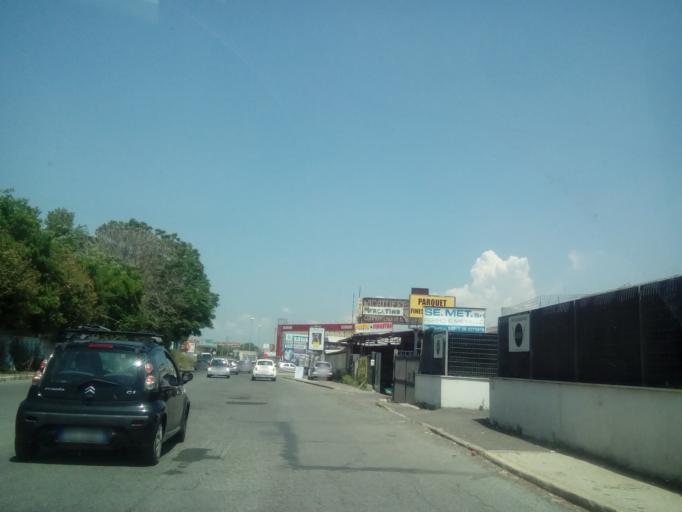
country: IT
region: Latium
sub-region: Citta metropolitana di Roma Capitale
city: Rome
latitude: 41.9159
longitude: 12.5620
